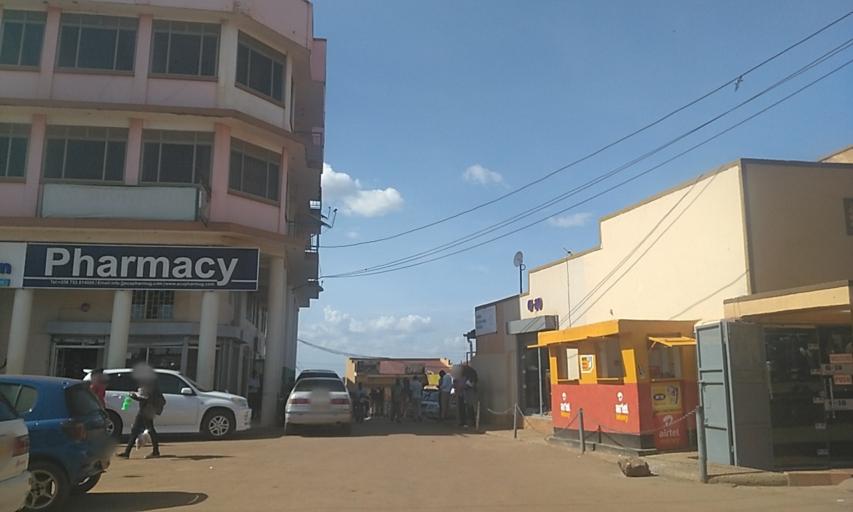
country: UG
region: Central Region
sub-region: Wakiso District
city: Kireka
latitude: 0.3551
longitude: 32.6130
